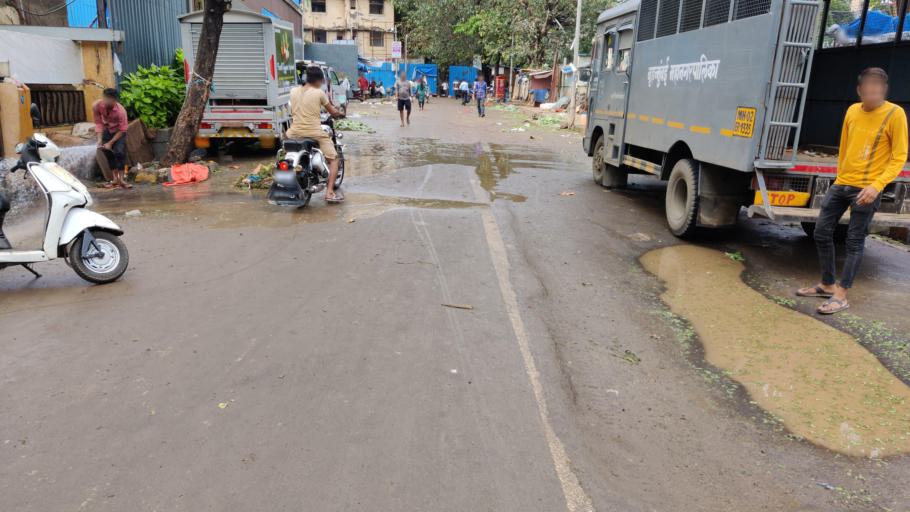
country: IN
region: Maharashtra
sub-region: Mumbai Suburban
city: Borivli
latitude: 19.2488
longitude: 72.8599
